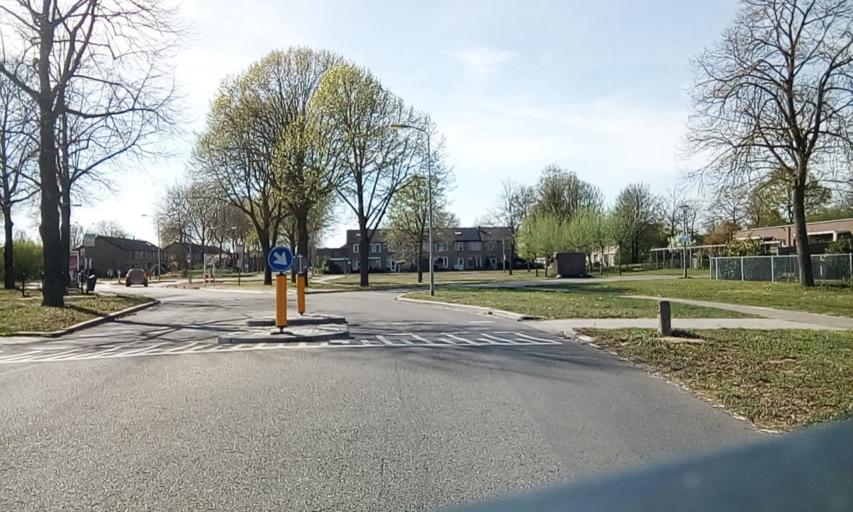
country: NL
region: Gelderland
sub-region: Gemeente Wijchen
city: Wijchen
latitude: 51.8151
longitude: 5.7220
